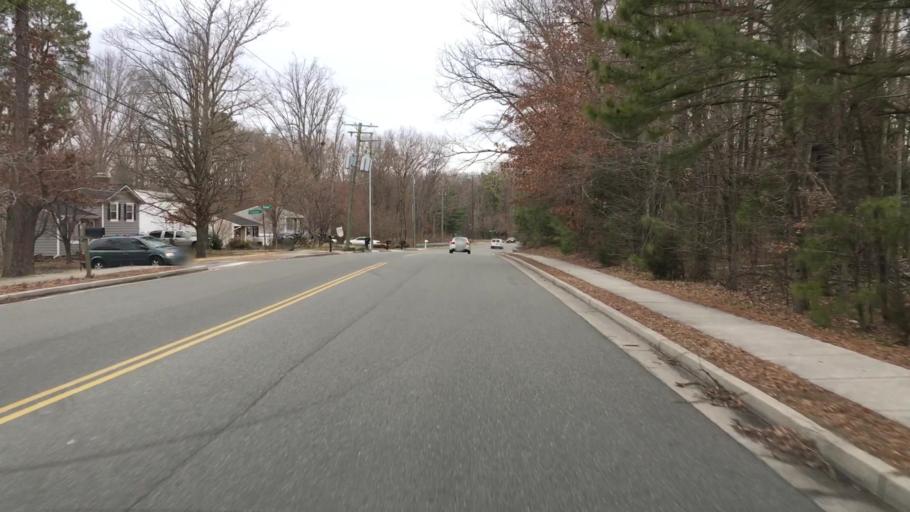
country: US
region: Virginia
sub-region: Henrico County
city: Laurel
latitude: 37.6501
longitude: -77.5472
